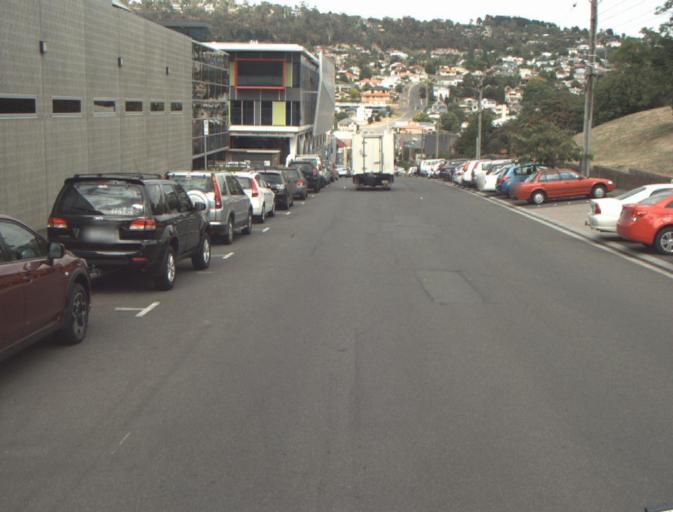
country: AU
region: Tasmania
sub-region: Launceston
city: Launceston
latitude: -41.4457
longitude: 147.1422
